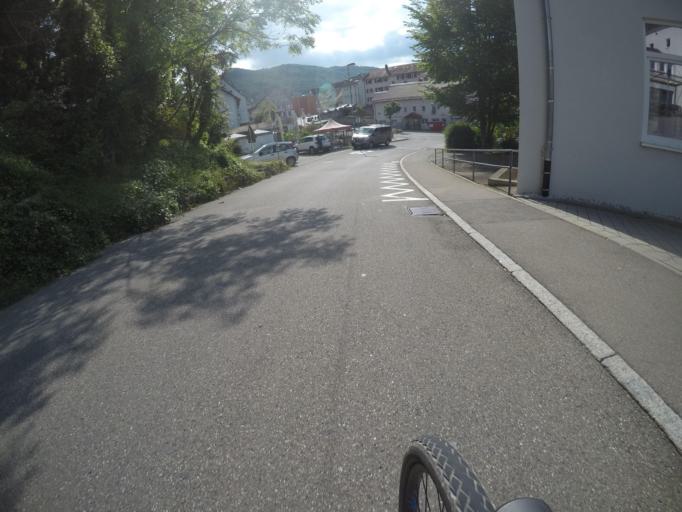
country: DE
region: Baden-Wuerttemberg
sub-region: Tuebingen Region
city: Bad Urach
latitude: 48.4953
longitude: 9.3963
